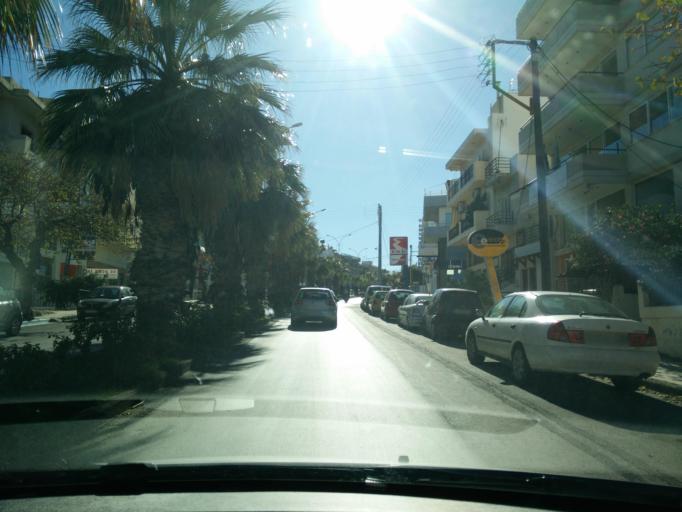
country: GR
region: Crete
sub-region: Nomos Irakleiou
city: Irakleion
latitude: 35.3361
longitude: 25.1419
